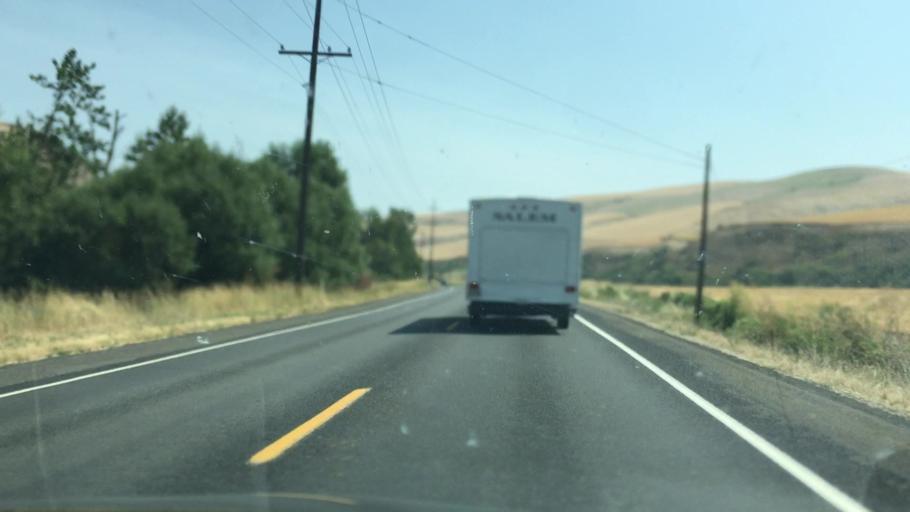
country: US
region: Idaho
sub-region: Nez Perce County
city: Lapwai
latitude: 46.3575
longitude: -116.7732
